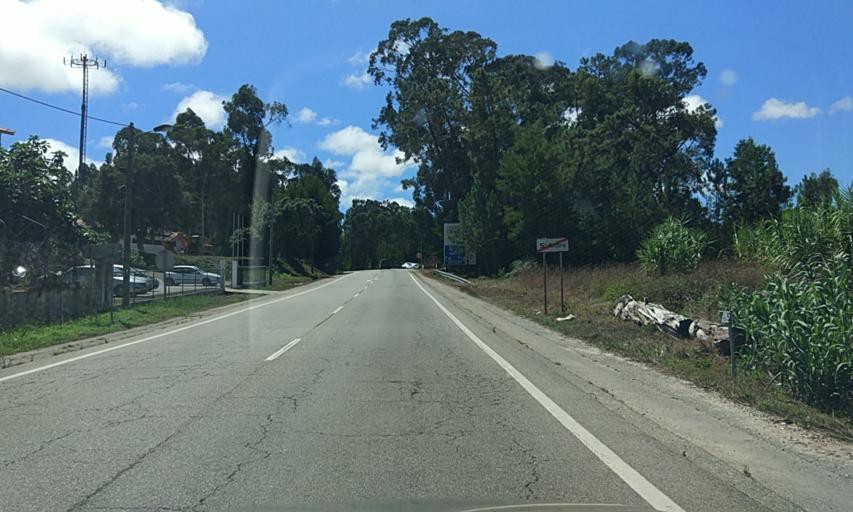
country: PT
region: Aveiro
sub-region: Vagos
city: Vagos
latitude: 40.5074
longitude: -8.6783
